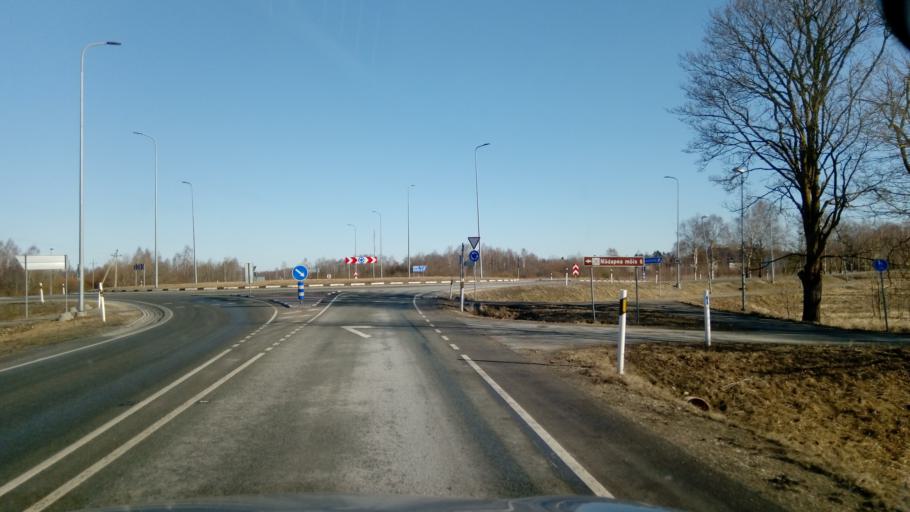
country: EE
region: Laeaene-Virumaa
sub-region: Rakvere linn
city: Rakvere
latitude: 59.3394
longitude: 26.3427
